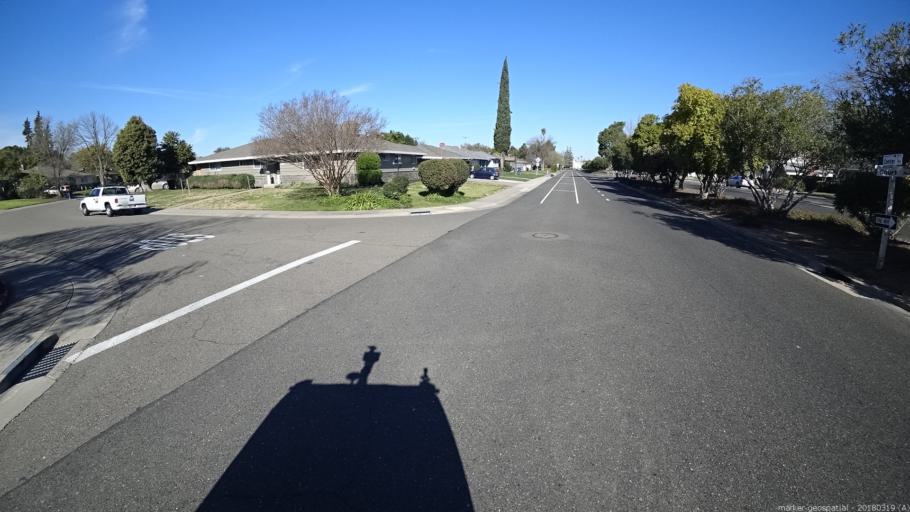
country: US
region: California
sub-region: Sacramento County
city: Parkway
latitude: 38.4906
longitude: -121.4507
